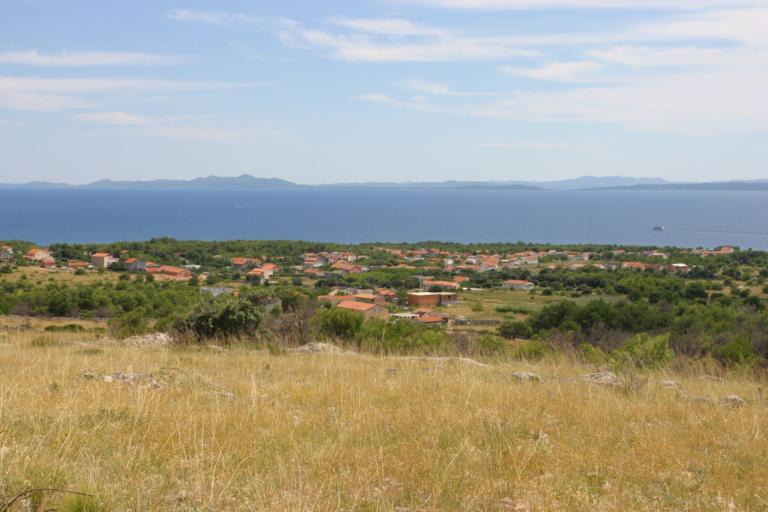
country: HR
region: Zadarska
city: Vir
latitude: 44.3014
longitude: 15.0522
